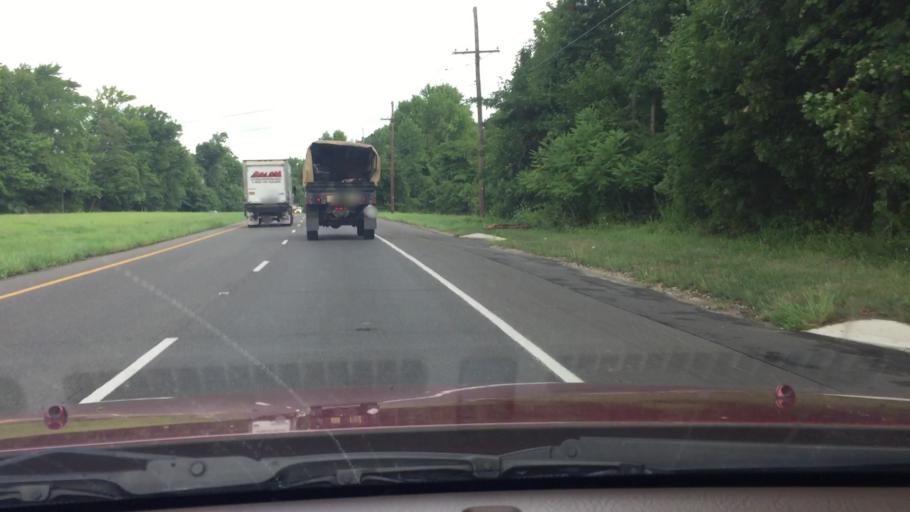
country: US
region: New Jersey
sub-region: Burlington County
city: Fort Dix
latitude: 40.0732
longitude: -74.6578
